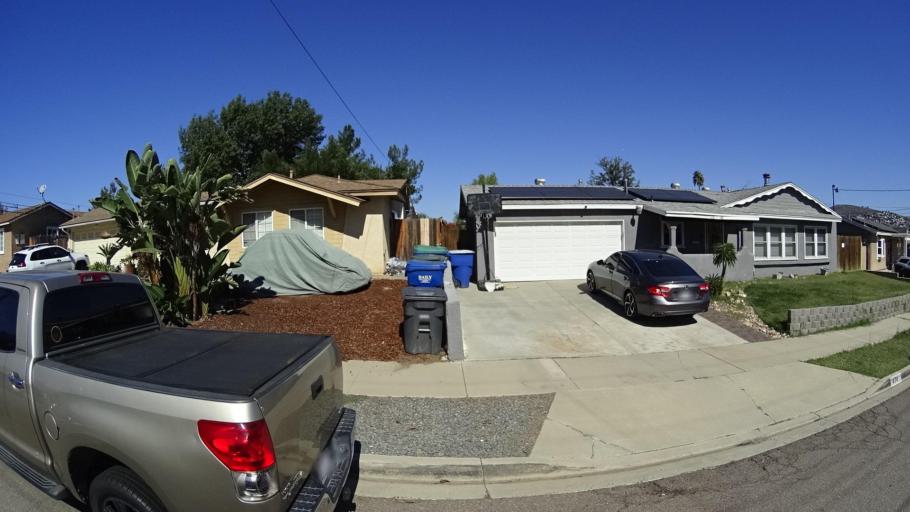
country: US
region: California
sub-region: San Diego County
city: La Presa
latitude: 32.7022
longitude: -117.0142
